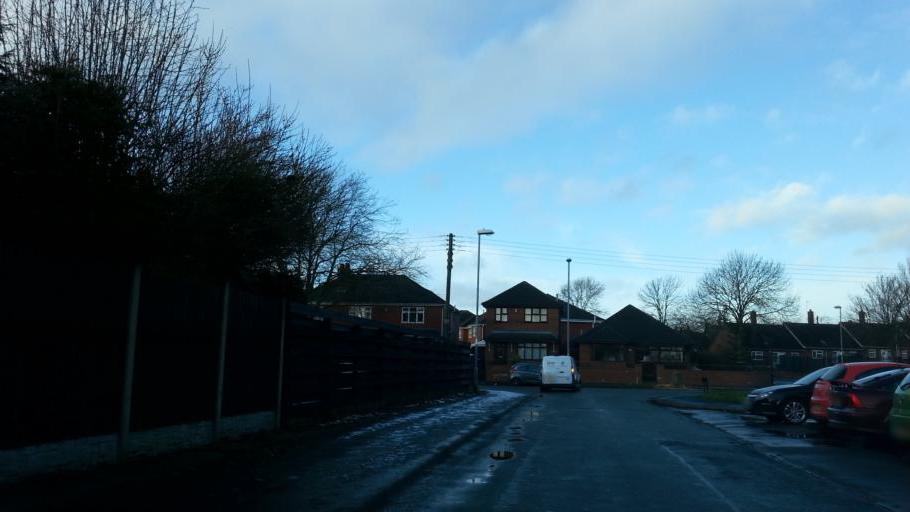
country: GB
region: England
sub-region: Staffordshire
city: Longton
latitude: 52.9836
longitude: -2.1507
